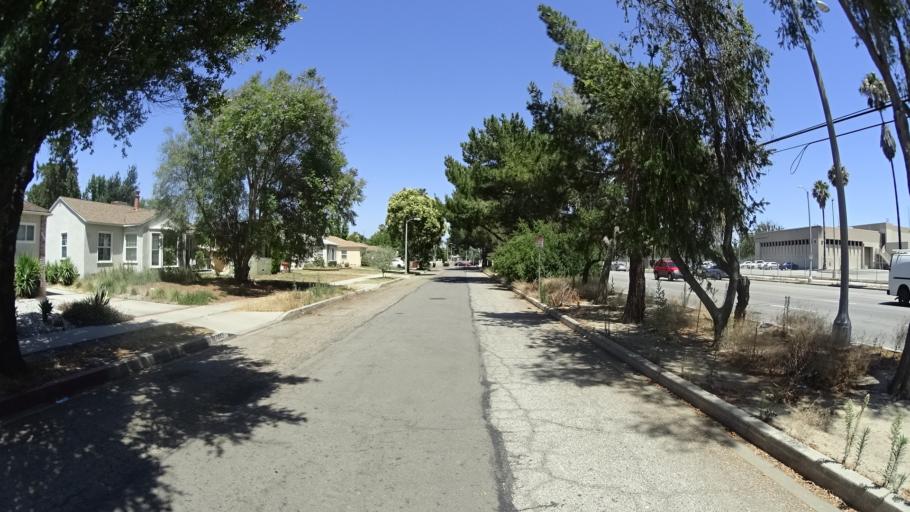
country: US
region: California
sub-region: Los Angeles County
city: Northridge
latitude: 34.1868
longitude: -118.5112
